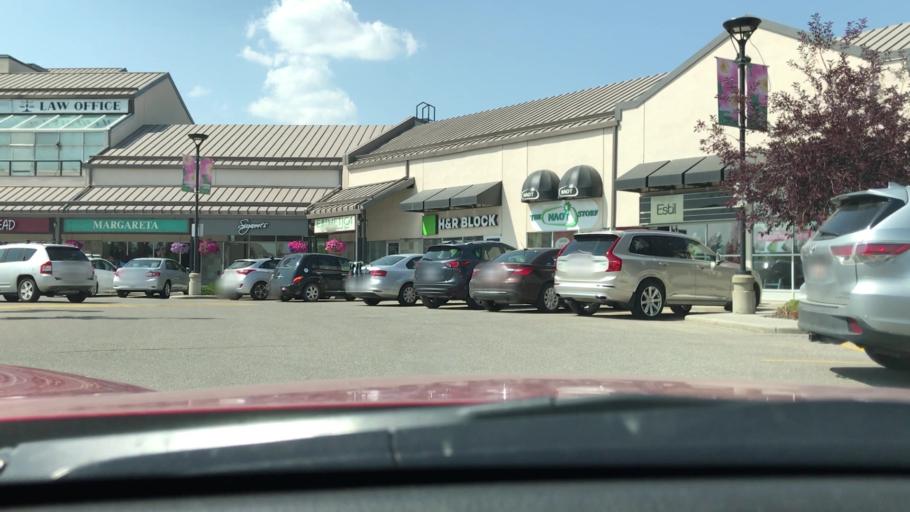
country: CA
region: Alberta
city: Calgary
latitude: 50.9741
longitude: -114.0980
